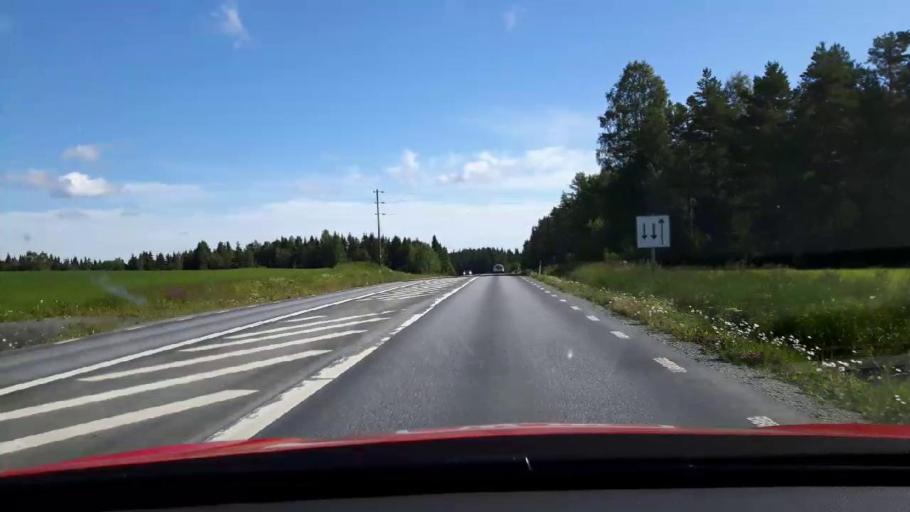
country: SE
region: Jaemtland
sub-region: OEstersunds Kommun
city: Lit
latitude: 63.2401
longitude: 14.7774
